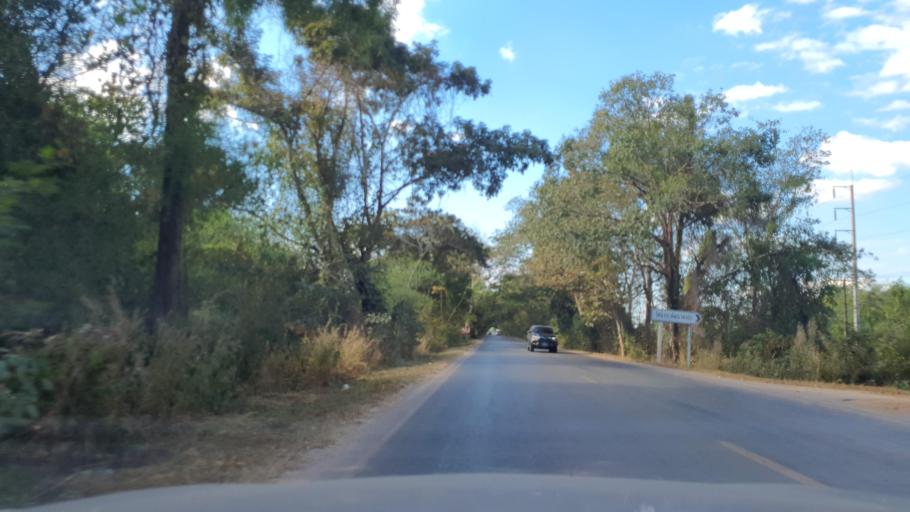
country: TH
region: Nakhon Phanom
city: Ban Phaeng
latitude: 18.0208
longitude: 104.1502
